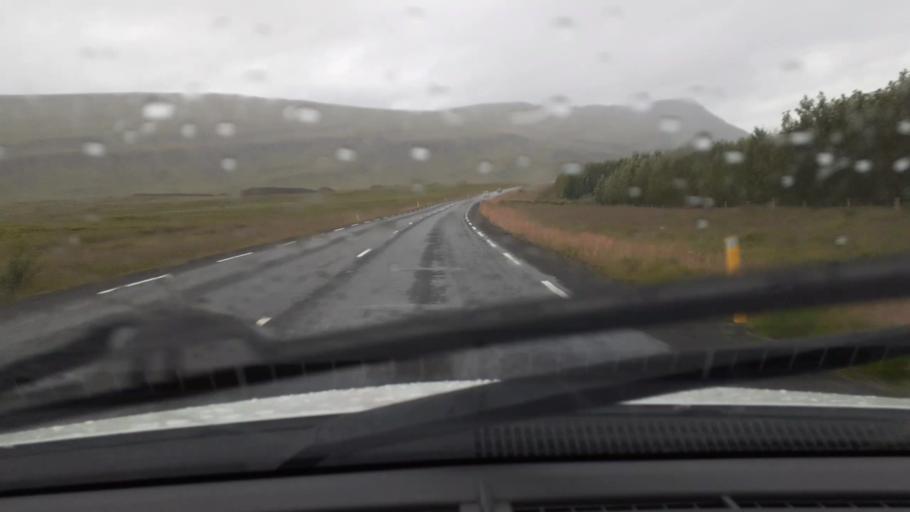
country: IS
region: West
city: Borgarnes
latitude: 64.3726
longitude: -21.8568
